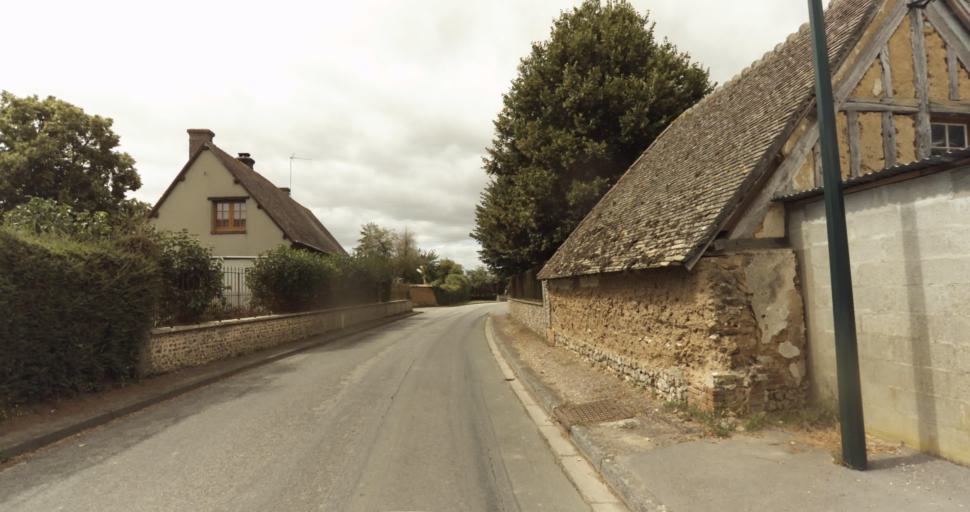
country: FR
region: Haute-Normandie
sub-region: Departement de l'Eure
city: Evreux
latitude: 48.9140
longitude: 1.2128
